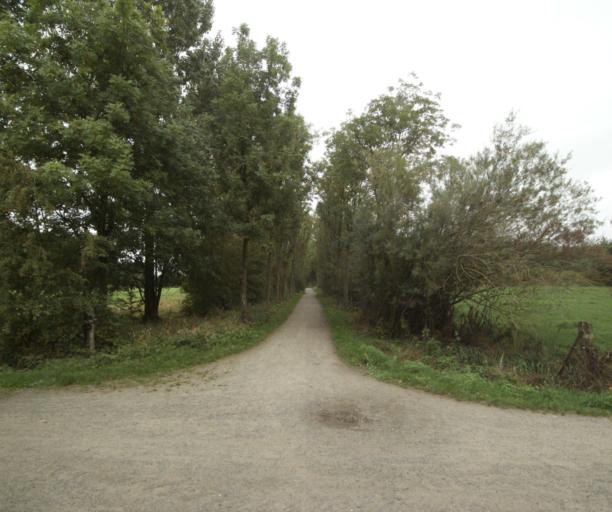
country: FR
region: Nord-Pas-de-Calais
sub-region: Departement du Nord
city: Chereng
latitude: 50.6265
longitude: 3.2115
